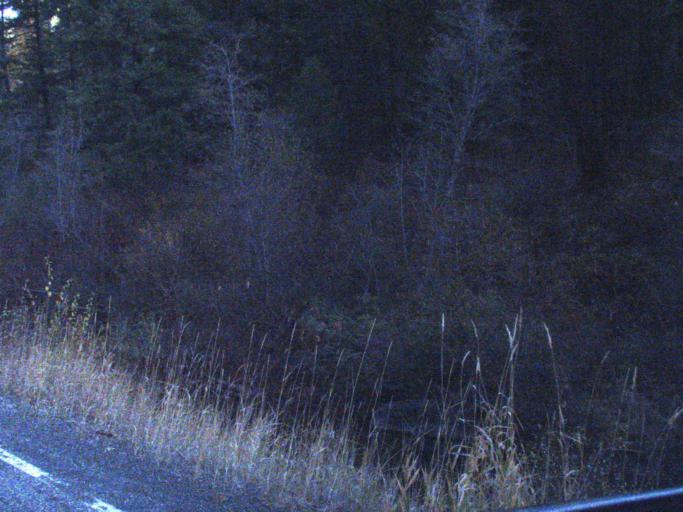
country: US
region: Washington
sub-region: Ferry County
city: Republic
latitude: 48.4904
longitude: -118.7390
